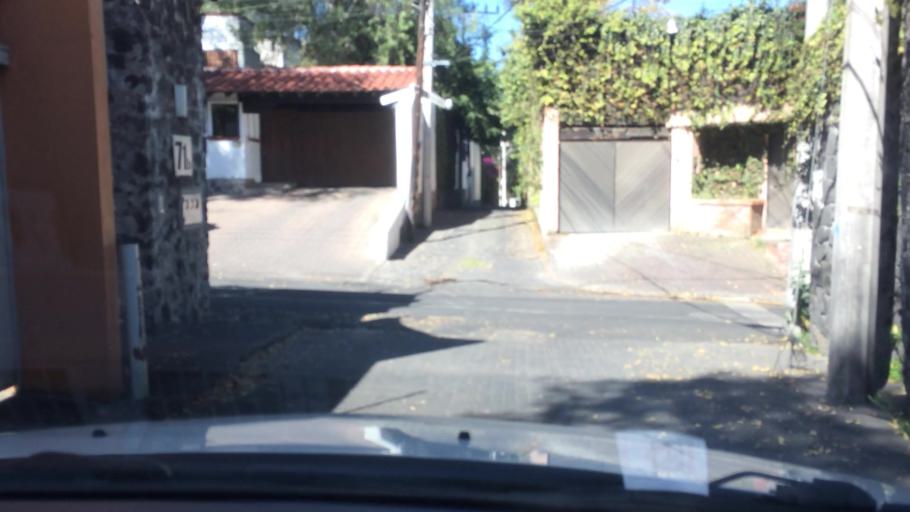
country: MX
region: Mexico City
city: Magdalena Contreras
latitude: 19.3271
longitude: -99.2214
